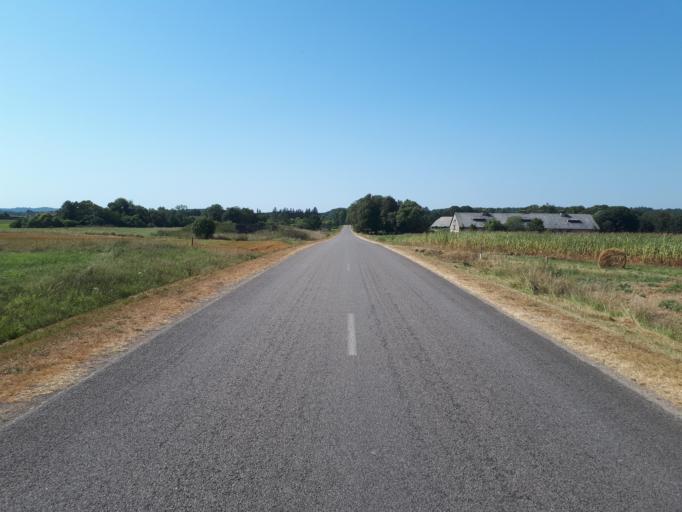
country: LT
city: Varniai
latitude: 55.8941
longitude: 22.4730
